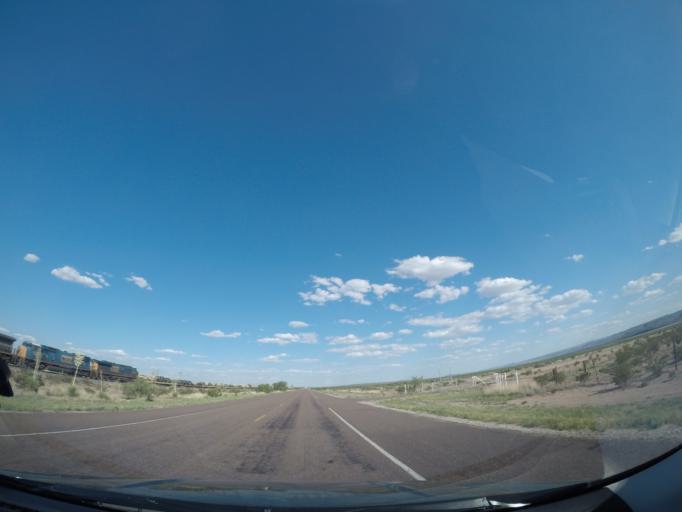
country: US
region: Texas
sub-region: Culberson County
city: Van Horn
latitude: 30.7142
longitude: -104.6586
